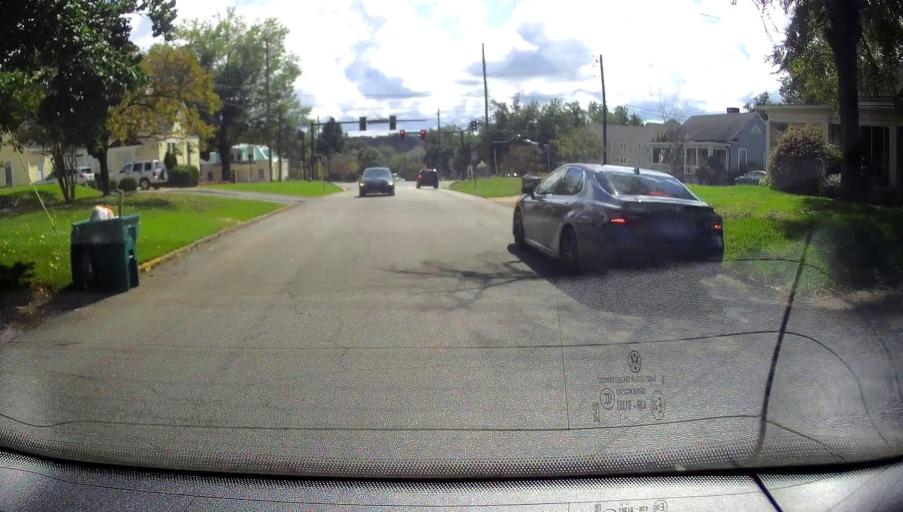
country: US
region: Georgia
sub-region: Baldwin County
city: Milledgeville
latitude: 33.0804
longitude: -83.2339
